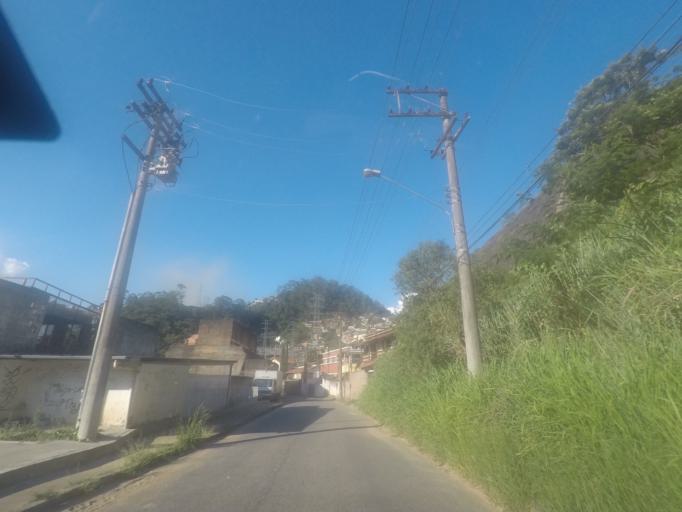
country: BR
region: Rio de Janeiro
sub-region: Petropolis
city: Petropolis
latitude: -22.4876
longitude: -43.1505
